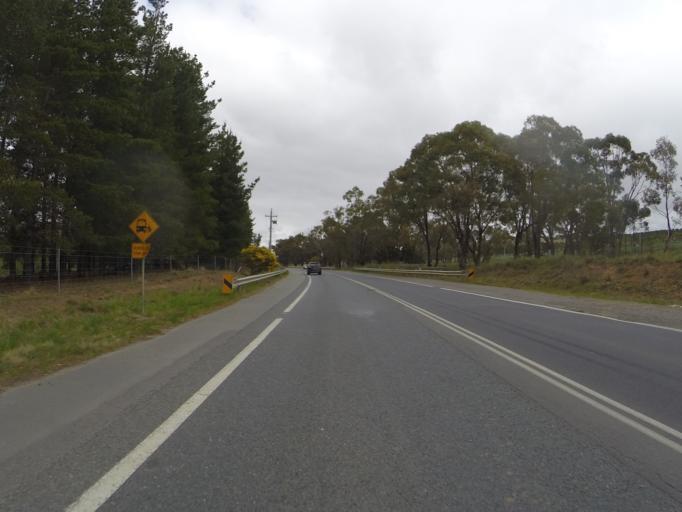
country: AU
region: Australian Capital Territory
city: Canberra
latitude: -35.2455
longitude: 149.1917
